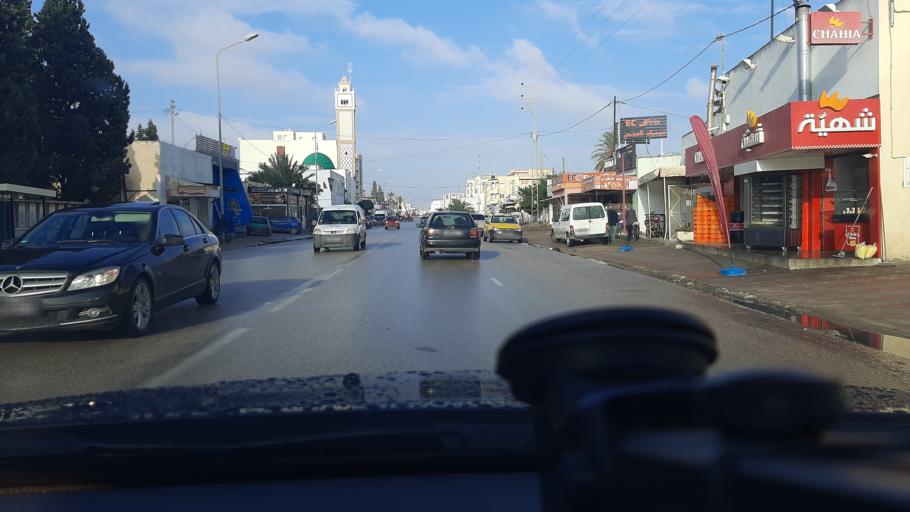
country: TN
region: Safaqis
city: Sfax
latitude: 34.7445
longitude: 10.7295
